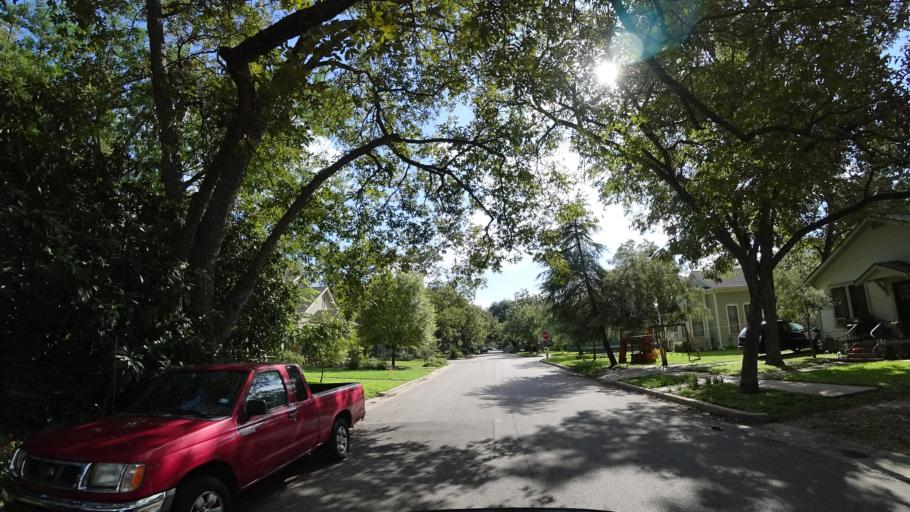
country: US
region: Texas
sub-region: Travis County
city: Austin
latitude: 30.3088
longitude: -97.7307
